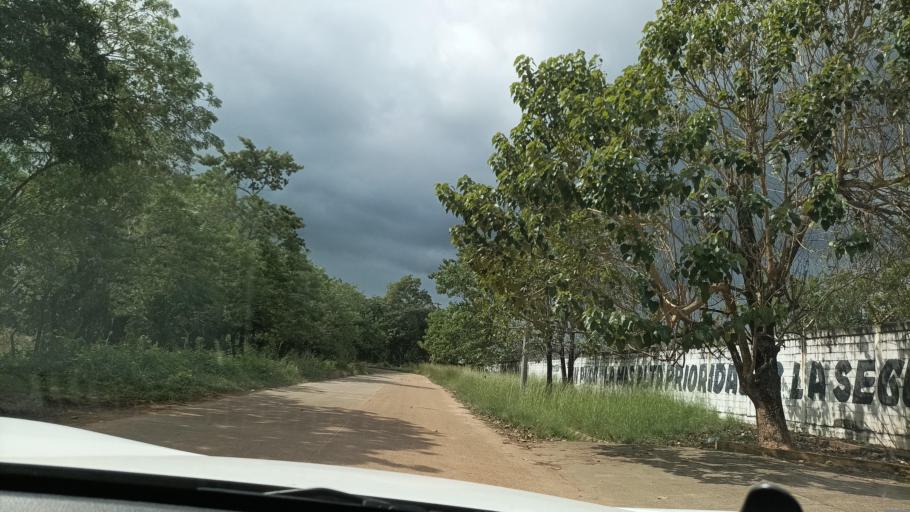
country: MX
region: Veracruz
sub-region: Chinameca
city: Chacalapa
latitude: 18.0780
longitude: -94.6908
